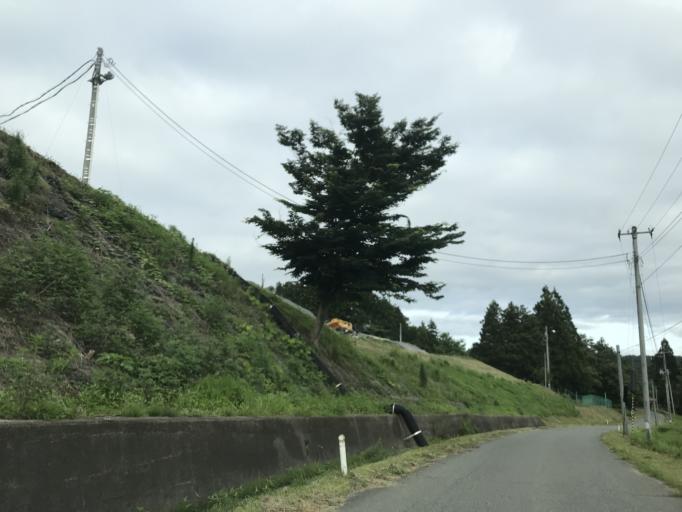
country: JP
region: Iwate
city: Ichinoseki
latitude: 38.8279
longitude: 141.2278
